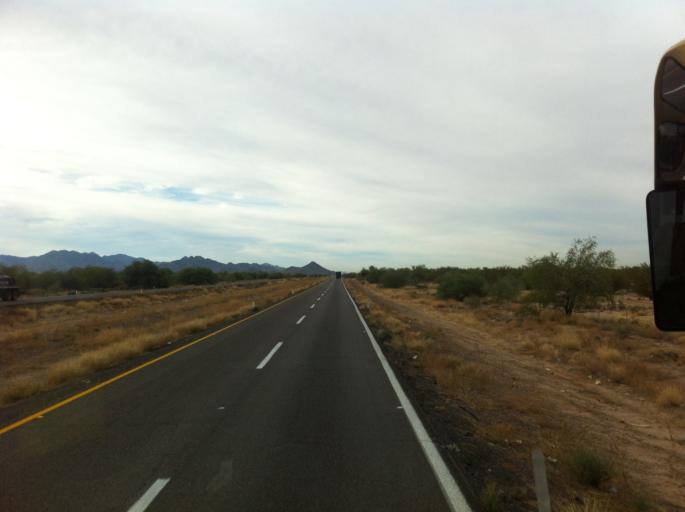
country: MX
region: Sonora
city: Hermosillo
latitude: 28.7256
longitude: -110.9802
